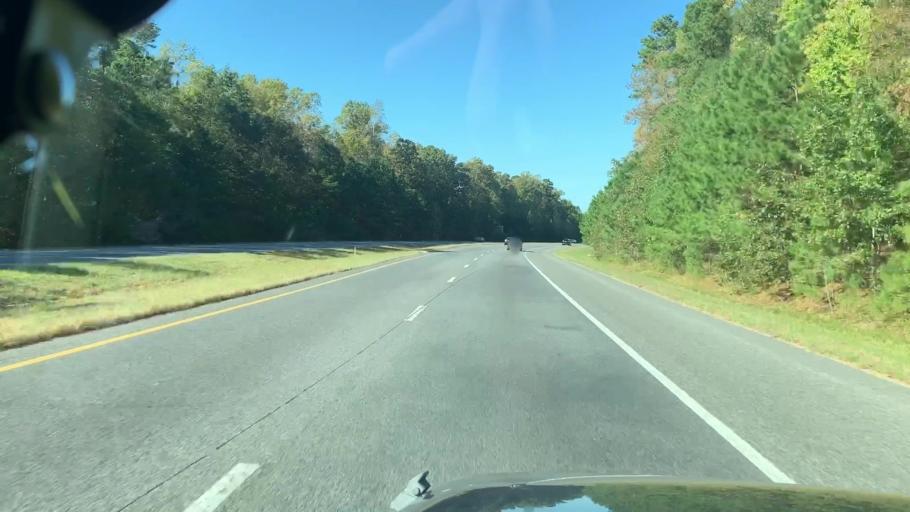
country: US
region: Virginia
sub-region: James City County
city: Williamsburg
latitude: 37.3144
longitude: -76.7487
